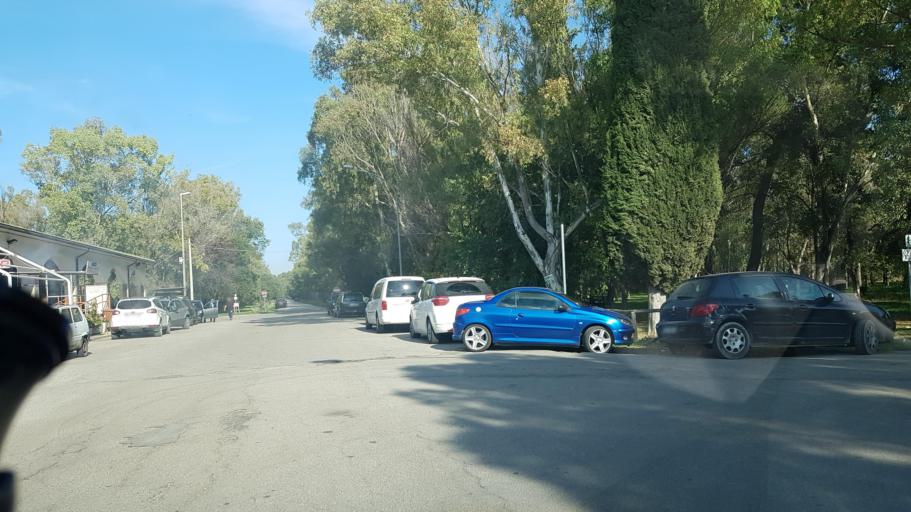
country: IT
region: Apulia
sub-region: Provincia di Foggia
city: Carapelle
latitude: 41.3836
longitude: 15.6429
